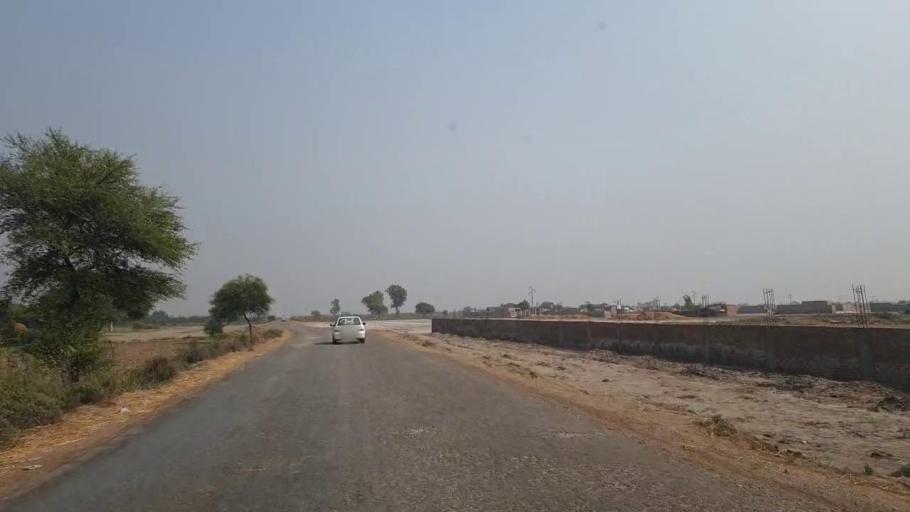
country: PK
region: Sindh
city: Matli
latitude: 25.0591
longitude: 68.6393
